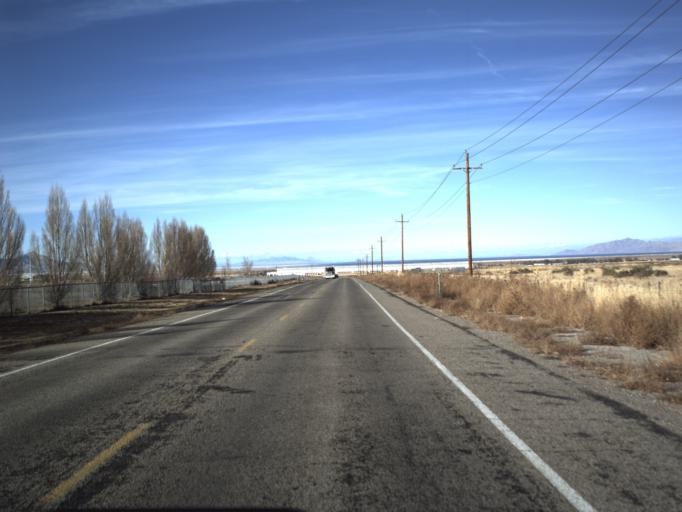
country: US
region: Utah
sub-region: Tooele County
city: Erda
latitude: 40.5721
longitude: -112.3673
